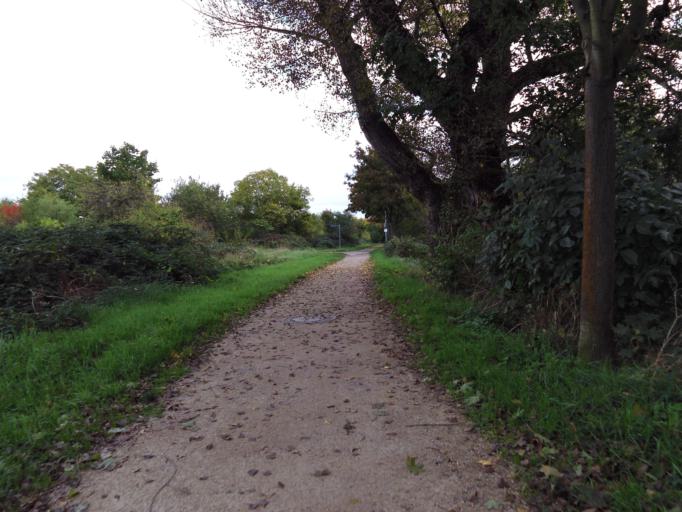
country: DE
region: Rheinland-Pfalz
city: Worms
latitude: 49.6382
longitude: 8.3411
